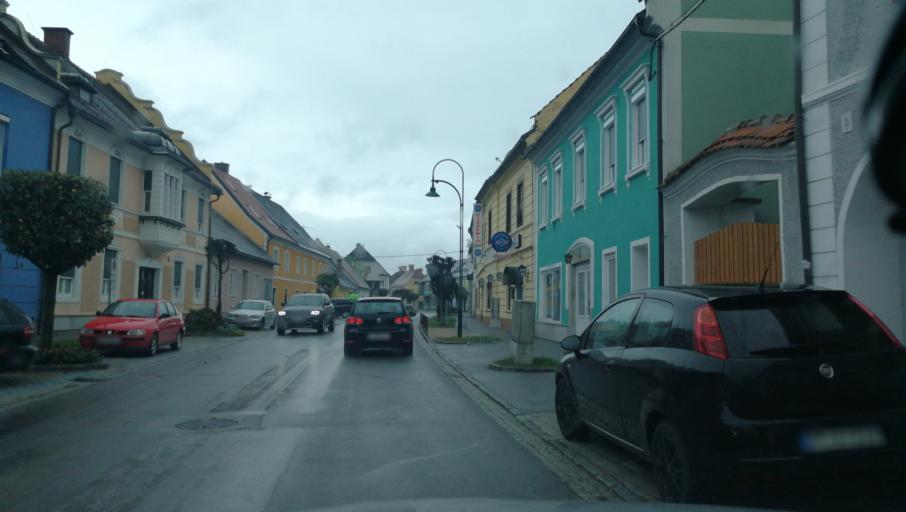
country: AT
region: Styria
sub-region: Politischer Bezirk Leibnitz
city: Strass in Steiermark
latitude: 46.7278
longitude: 15.6223
